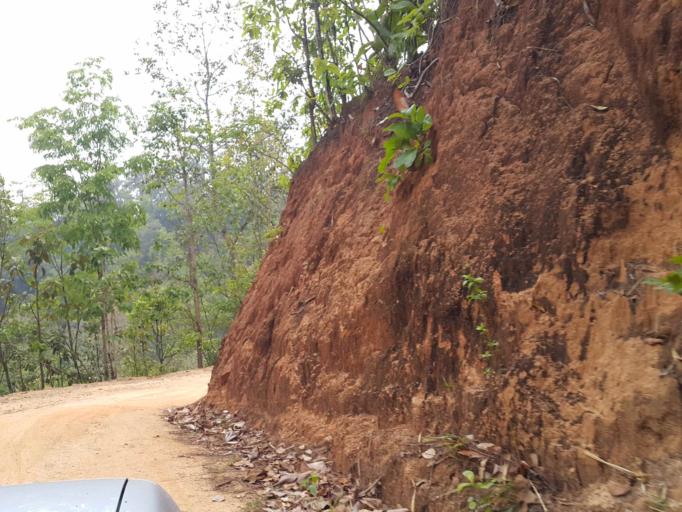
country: TH
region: Chiang Mai
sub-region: Amphoe Chiang Dao
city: Chiang Dao
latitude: 19.2952
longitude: 98.7537
